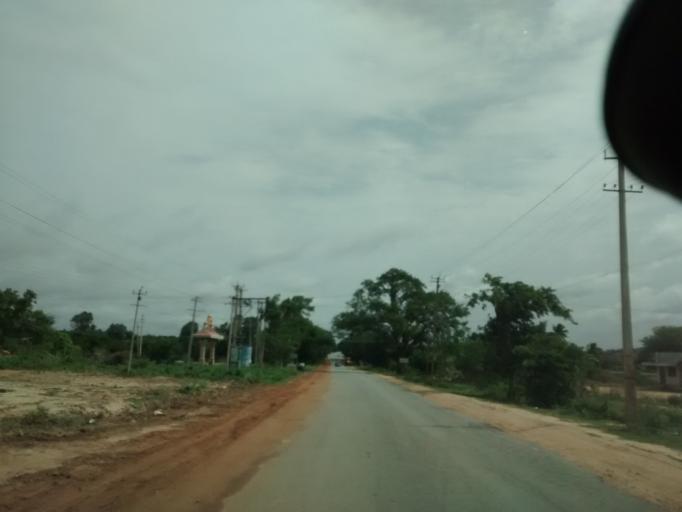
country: IN
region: Karnataka
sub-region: Tumkur
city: Koratagere
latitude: 13.5324
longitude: 77.2438
